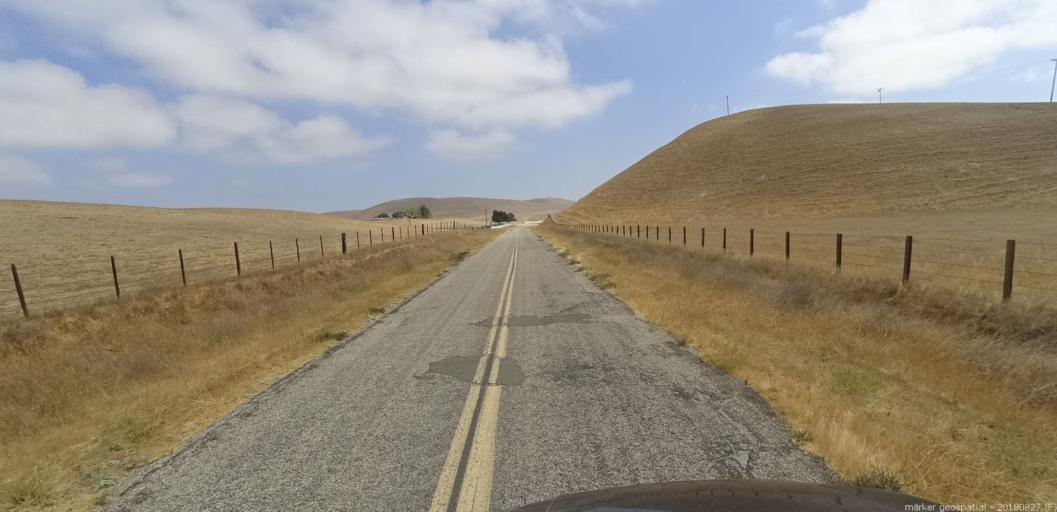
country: US
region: California
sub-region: Monterey County
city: King City
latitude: 36.2255
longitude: -121.0655
